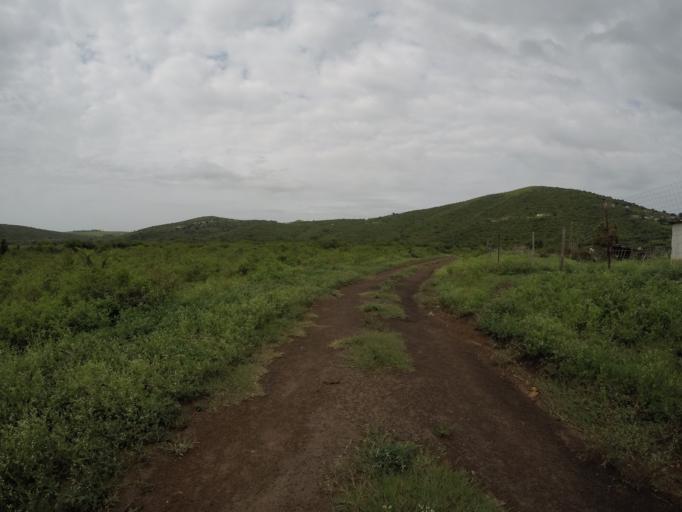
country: ZA
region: KwaZulu-Natal
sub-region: uThungulu District Municipality
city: Empangeni
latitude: -28.6423
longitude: 31.9028
